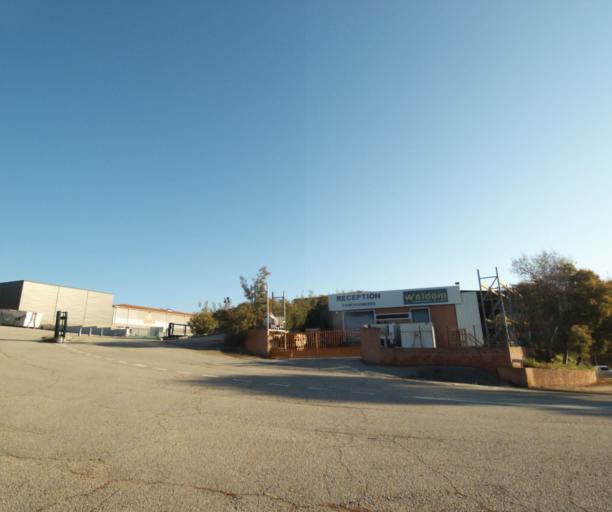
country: FR
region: Corsica
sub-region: Departement de la Corse-du-Sud
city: Propriano
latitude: 41.6668
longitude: 8.9179
